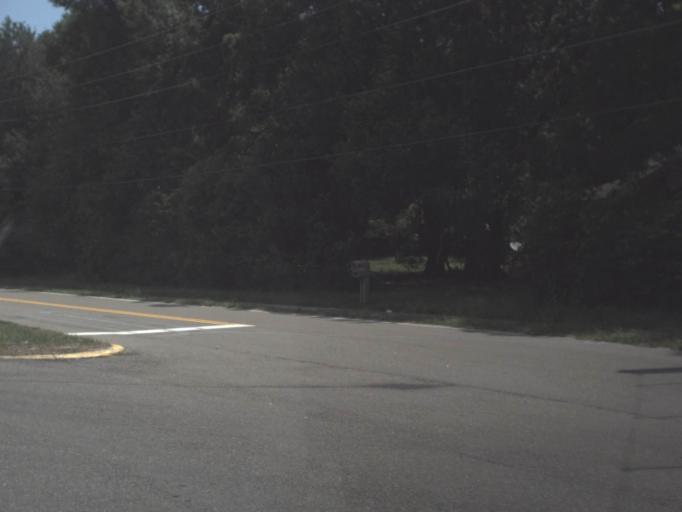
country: US
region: Florida
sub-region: Duval County
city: Jacksonville
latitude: 30.3129
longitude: -81.5587
